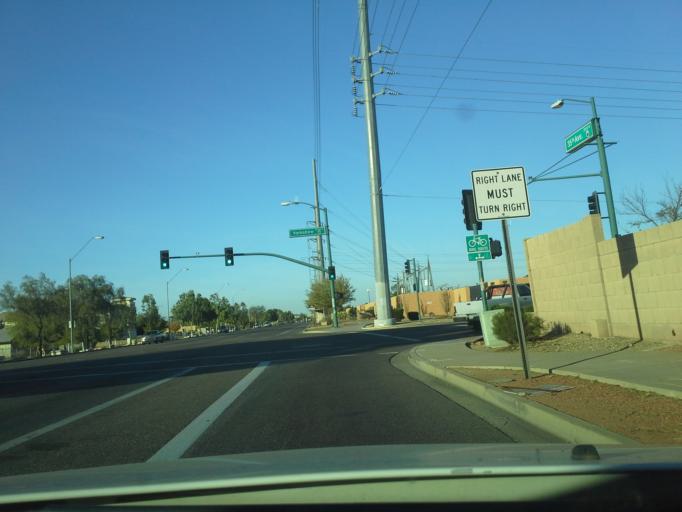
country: US
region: Arizona
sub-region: Maricopa County
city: Peoria
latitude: 33.6617
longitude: -112.1345
